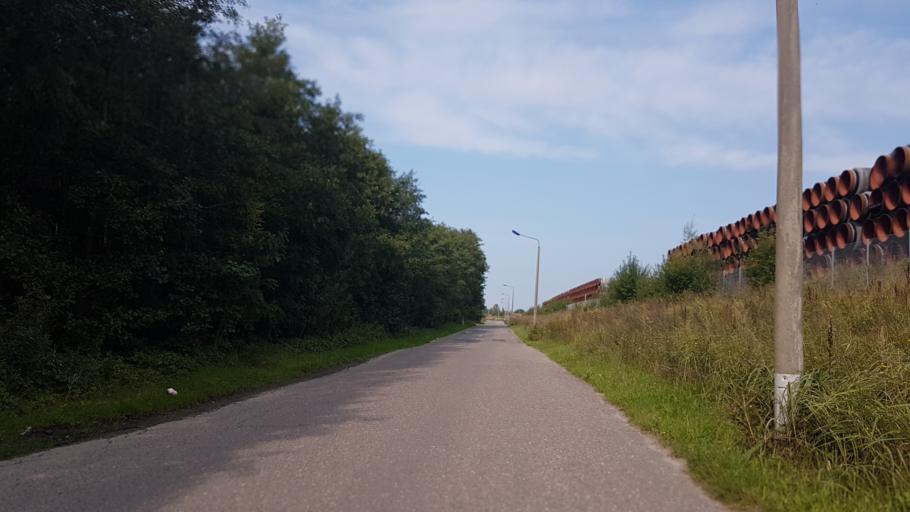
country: DE
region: Mecklenburg-Vorpommern
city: Sagard
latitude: 54.4897
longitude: 13.5728
